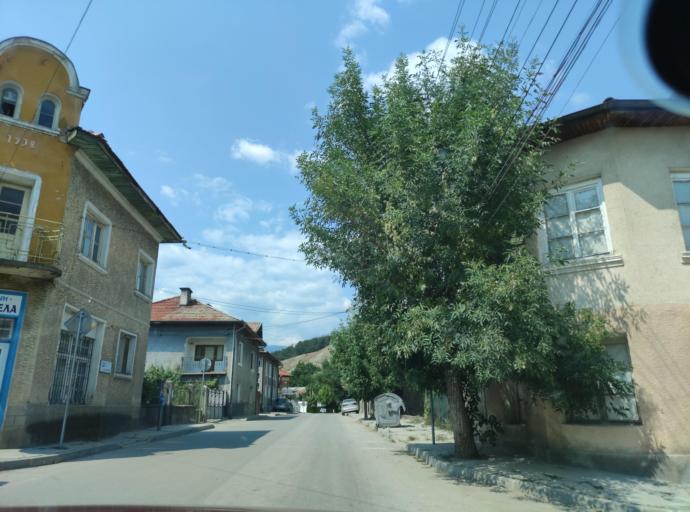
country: BG
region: Blagoevgrad
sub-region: Obshtina Belitsa
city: Belitsa
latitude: 41.9486
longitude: 23.5564
